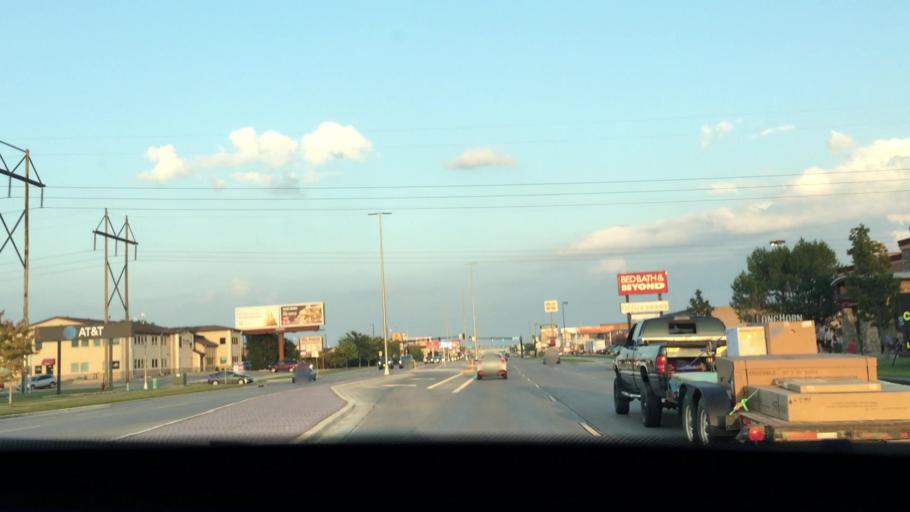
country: US
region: North Dakota
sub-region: Cass County
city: West Fargo
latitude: 46.8618
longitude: -96.8605
